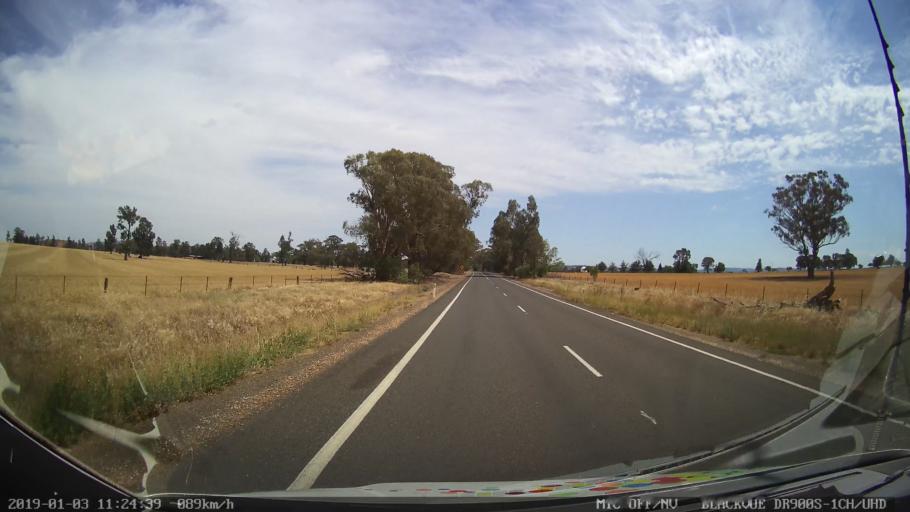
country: AU
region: New South Wales
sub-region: Weddin
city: Grenfell
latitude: -34.0488
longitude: 148.2336
